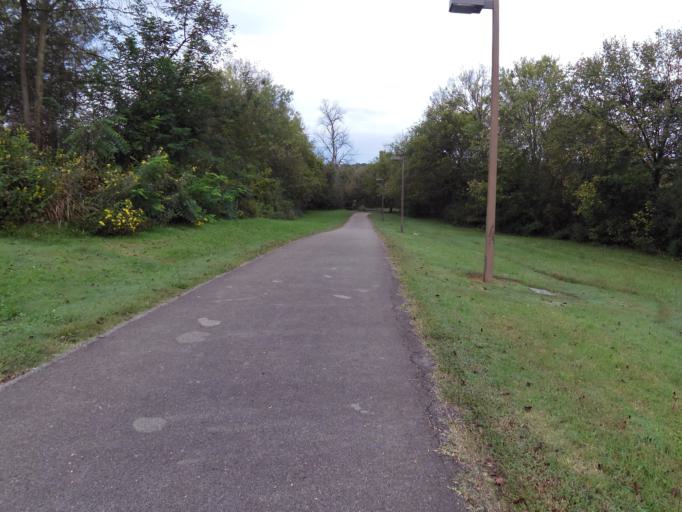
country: US
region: Tennessee
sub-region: Blount County
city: Eagleton Village
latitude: 35.8047
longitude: -83.9481
